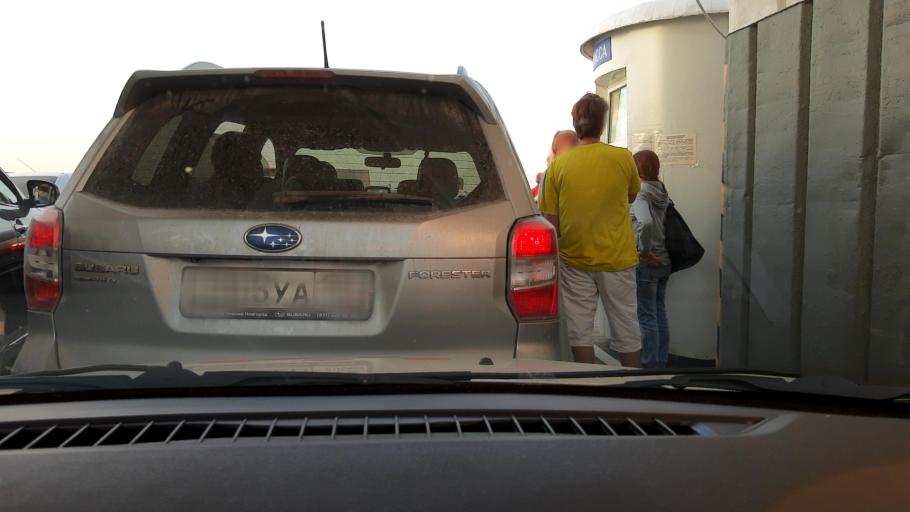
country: RU
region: Nizjnij Novgorod
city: Nizhniy Novgorod
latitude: 56.3332
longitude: 44.0237
